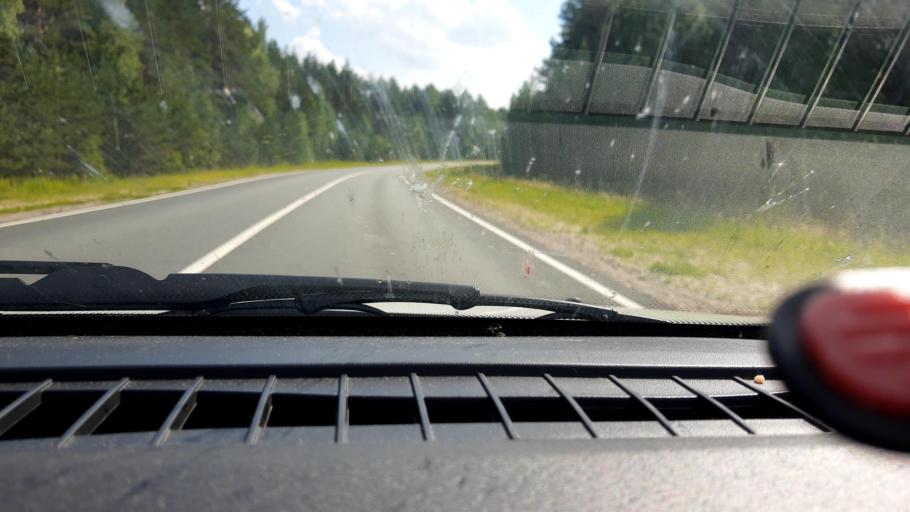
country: RU
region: Nizjnij Novgorod
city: Krasnyye Baki
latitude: 57.2056
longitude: 45.4610
